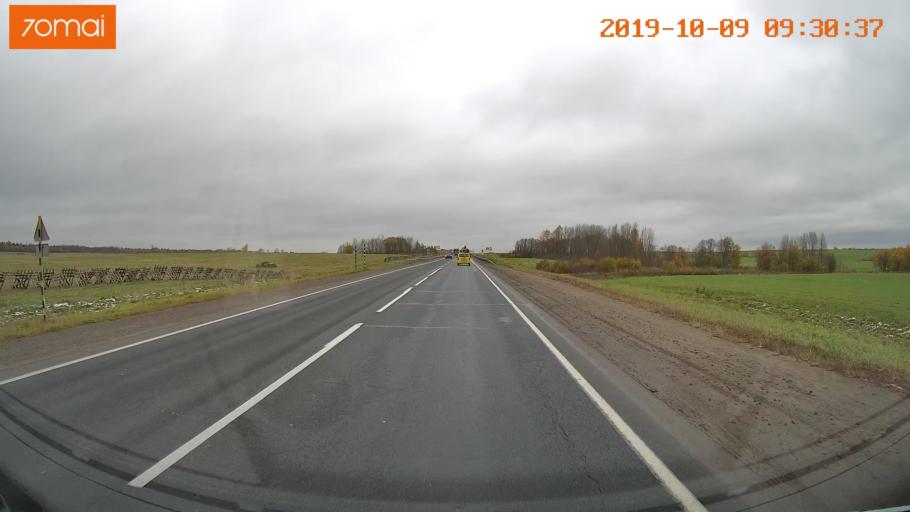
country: RU
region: Vologda
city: Vologda
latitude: 59.1415
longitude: 39.9472
